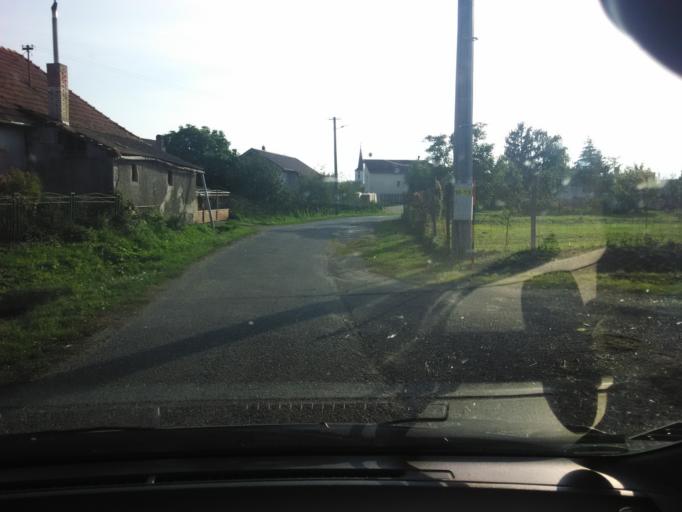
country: SK
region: Nitriansky
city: Levice
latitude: 48.2884
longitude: 18.6992
